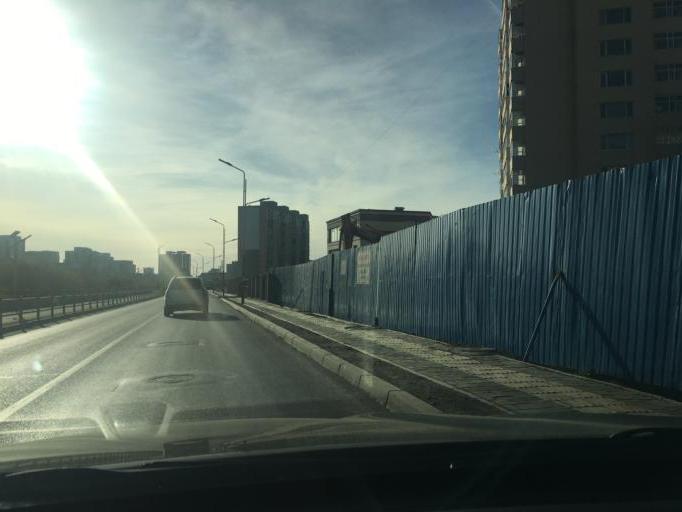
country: MN
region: Ulaanbaatar
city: Ulaanbaatar
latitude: 47.9050
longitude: 106.9056
